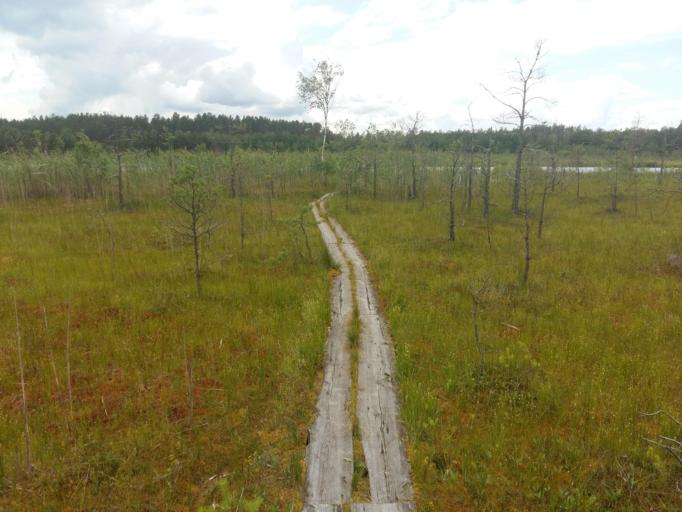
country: LT
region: Alytaus apskritis
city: Varena
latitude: 54.0251
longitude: 24.3569
